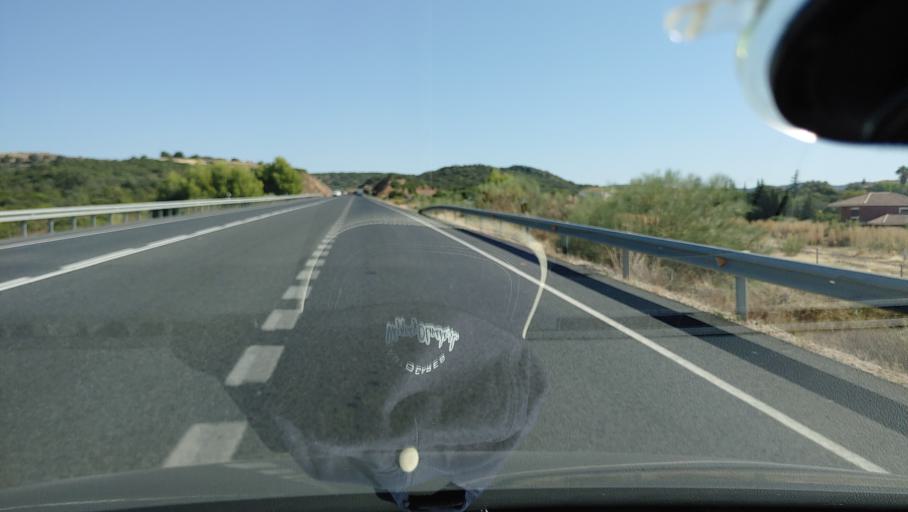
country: ES
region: Andalusia
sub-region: Province of Cordoba
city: Cordoba
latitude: 37.9330
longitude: -4.7653
